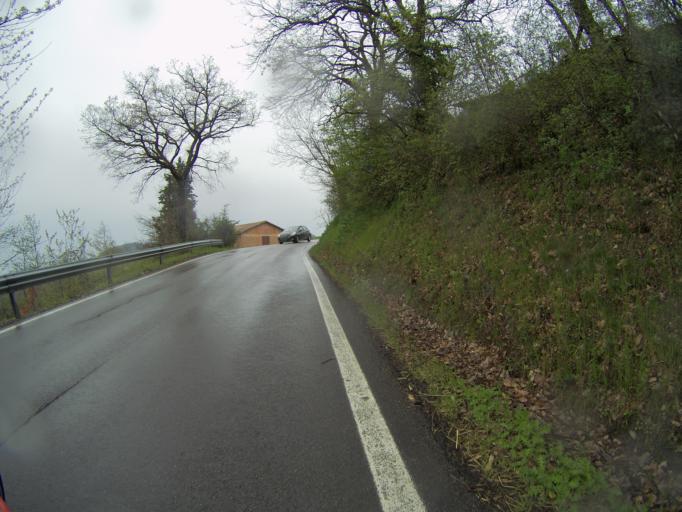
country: IT
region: Emilia-Romagna
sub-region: Provincia di Reggio Emilia
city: Ciano d'Enza
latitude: 44.5682
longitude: 10.4142
